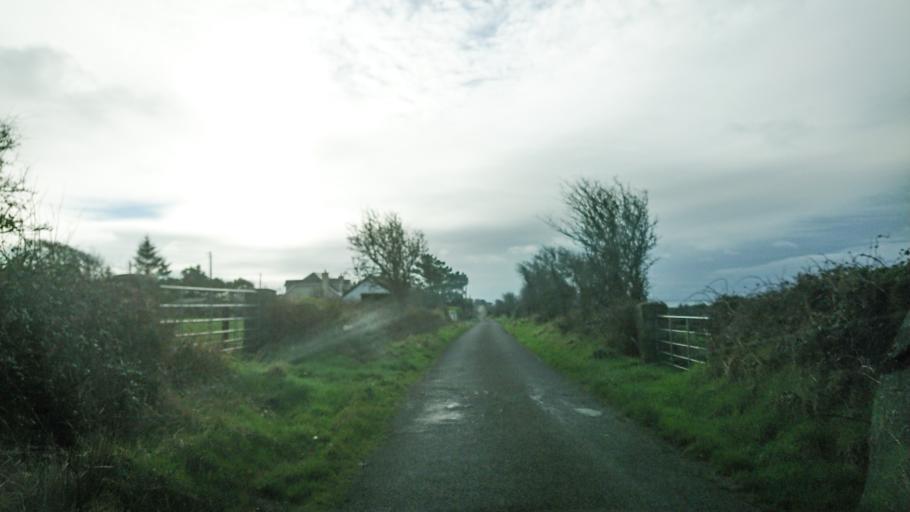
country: IE
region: Munster
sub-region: Waterford
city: Tra Mhor
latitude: 52.1482
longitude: -7.1928
